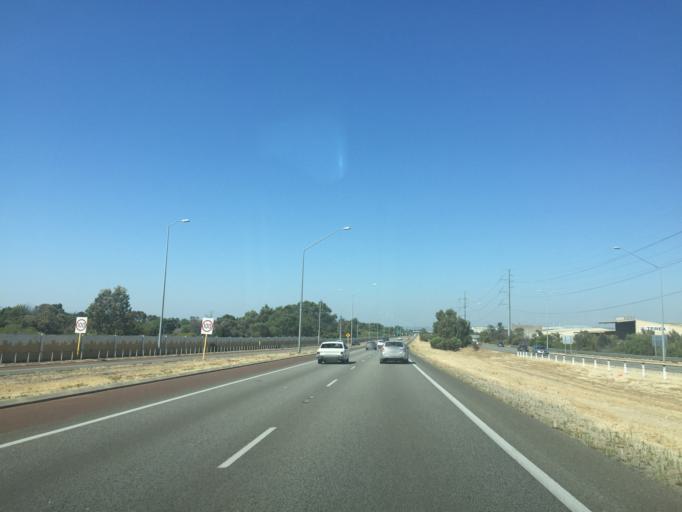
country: AU
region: Western Australia
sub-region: Canning
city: Willetton
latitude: -32.0667
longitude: 115.8926
